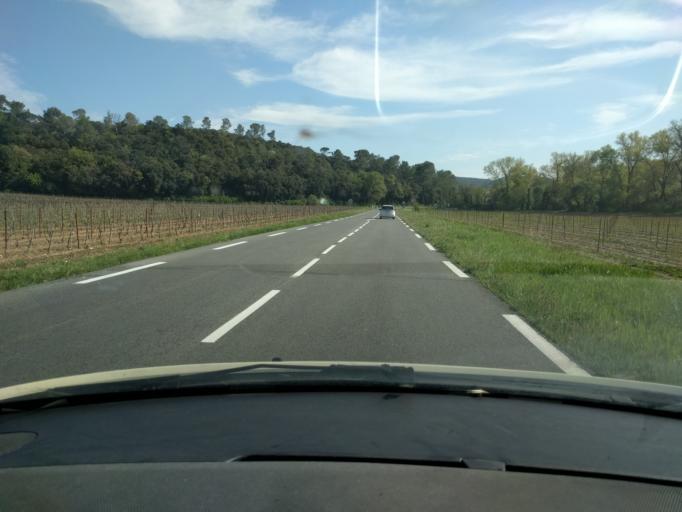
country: FR
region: Provence-Alpes-Cote d'Azur
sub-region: Departement du Var
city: Hyeres
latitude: 43.1570
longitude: 6.1284
